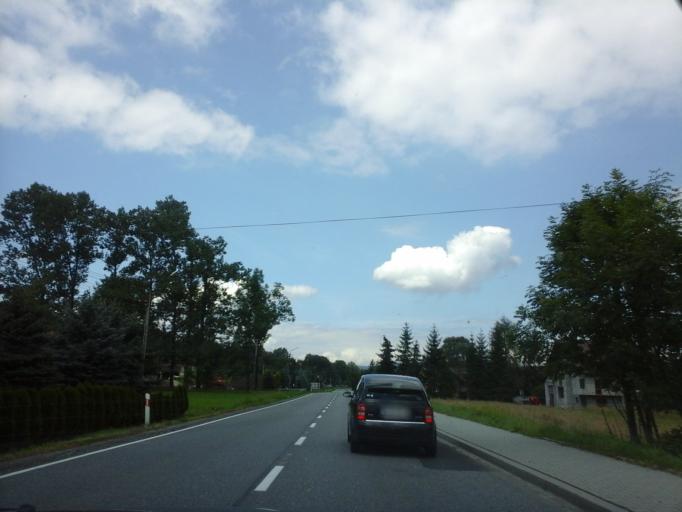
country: PL
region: Lesser Poland Voivodeship
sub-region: Powiat suski
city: Juszczyn
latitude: 49.7033
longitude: 19.6972
